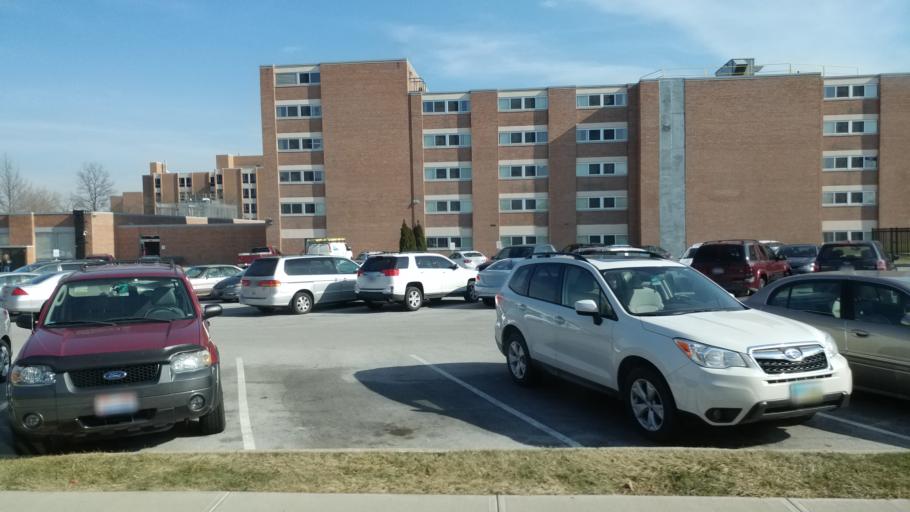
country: US
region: Ohio
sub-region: Wood County
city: Bowling Green
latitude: 41.3792
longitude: -83.6429
